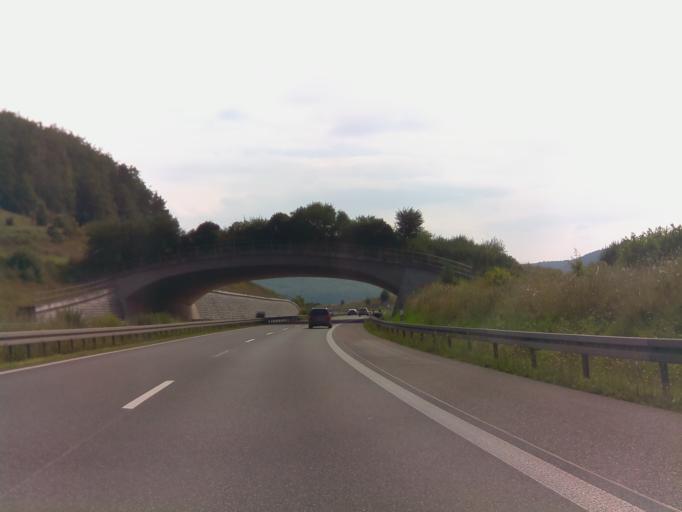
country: DE
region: Thuringia
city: Ellingshausen
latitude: 50.5433
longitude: 10.4788
